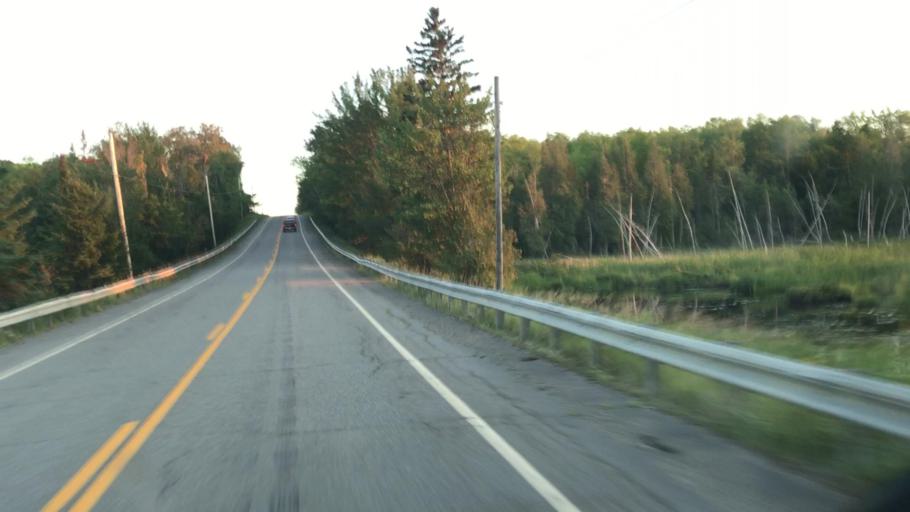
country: US
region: Maine
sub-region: Penobscot County
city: Medway
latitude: 45.5976
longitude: -68.3105
